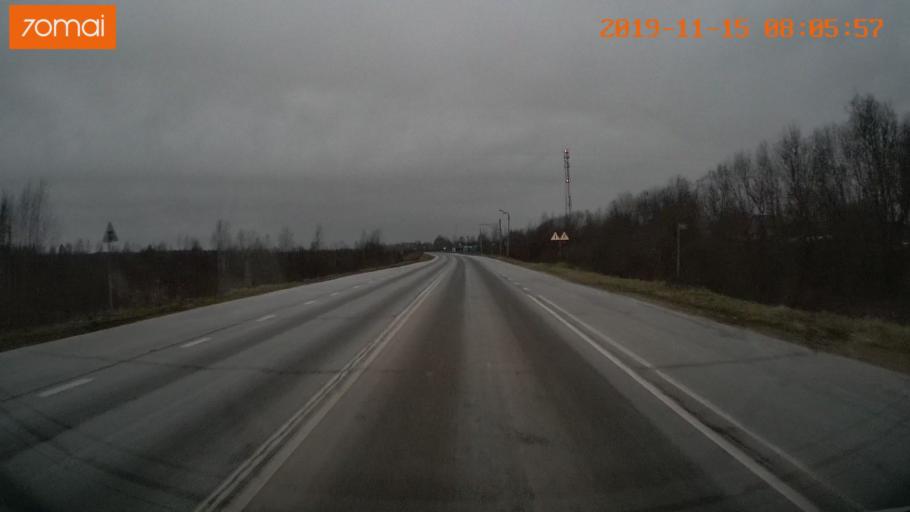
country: RU
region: Vologda
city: Cherepovets
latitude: 59.0196
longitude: 38.0479
